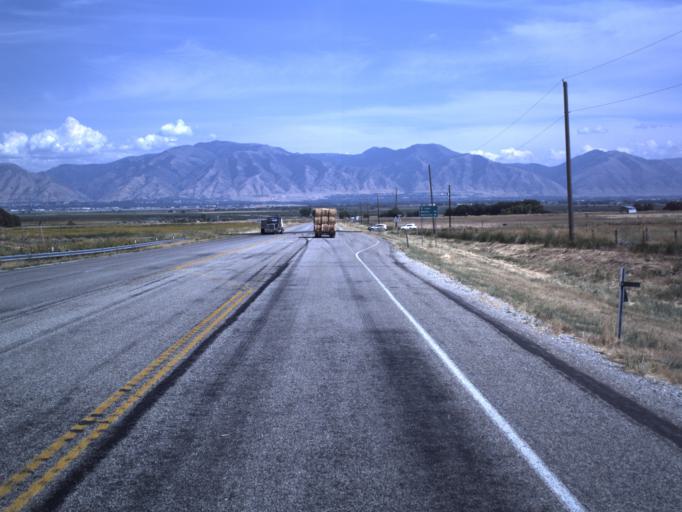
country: US
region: Utah
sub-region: Cache County
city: Mendon
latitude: 41.7513
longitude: -111.9819
